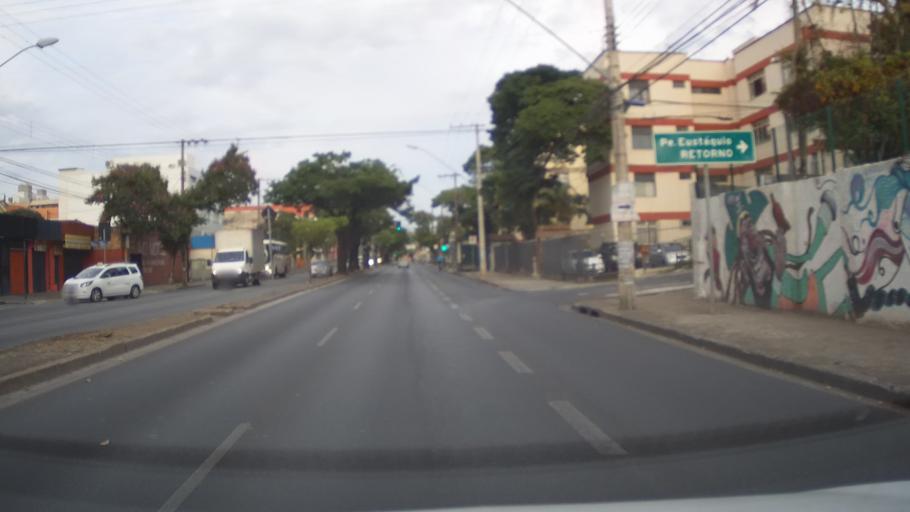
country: BR
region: Minas Gerais
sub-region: Belo Horizonte
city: Belo Horizonte
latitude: -19.9126
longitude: -43.9728
